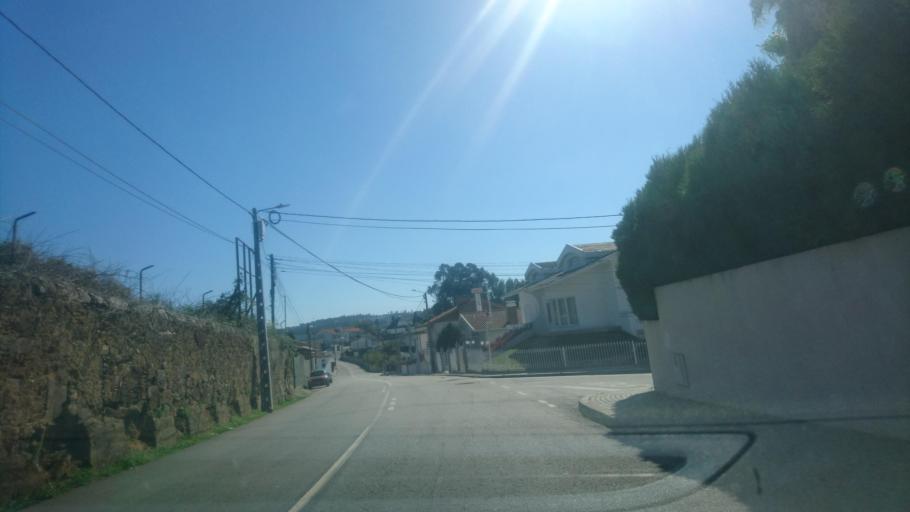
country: PT
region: Aveiro
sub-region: Santa Maria da Feira
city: Lamas
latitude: 40.9889
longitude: -8.5746
